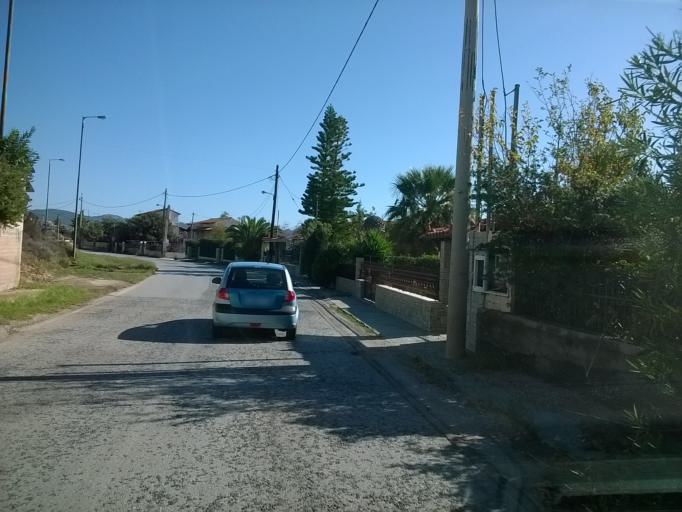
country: GR
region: Attica
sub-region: Nomarchia Anatolikis Attikis
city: Anavyssos
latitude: 37.7360
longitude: 23.9315
